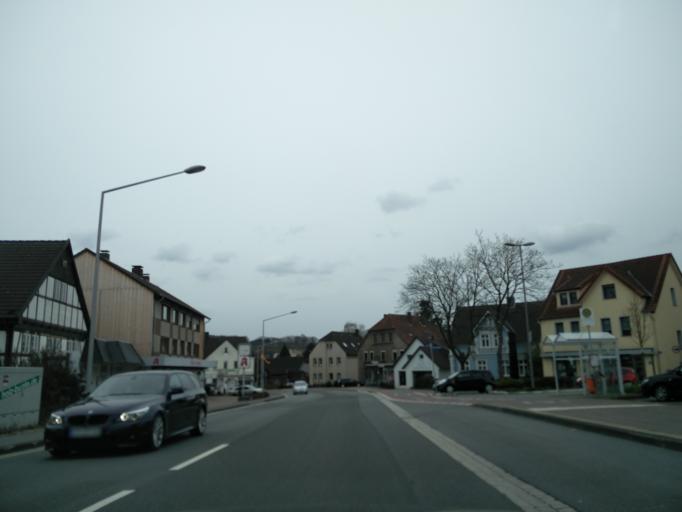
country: DE
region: North Rhine-Westphalia
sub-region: Regierungsbezirk Detmold
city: Detmold
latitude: 51.9219
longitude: 8.8996
